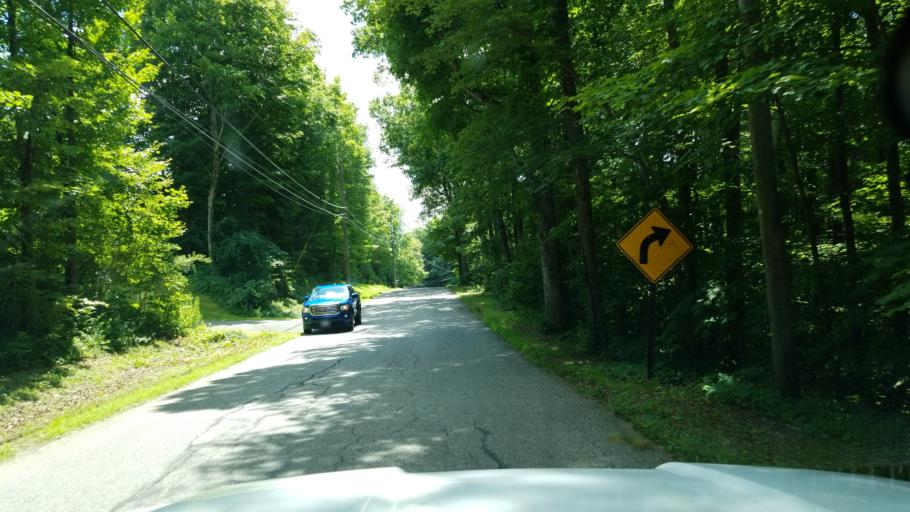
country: US
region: Massachusetts
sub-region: Hampden County
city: Holland
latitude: 41.9768
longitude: -72.1899
